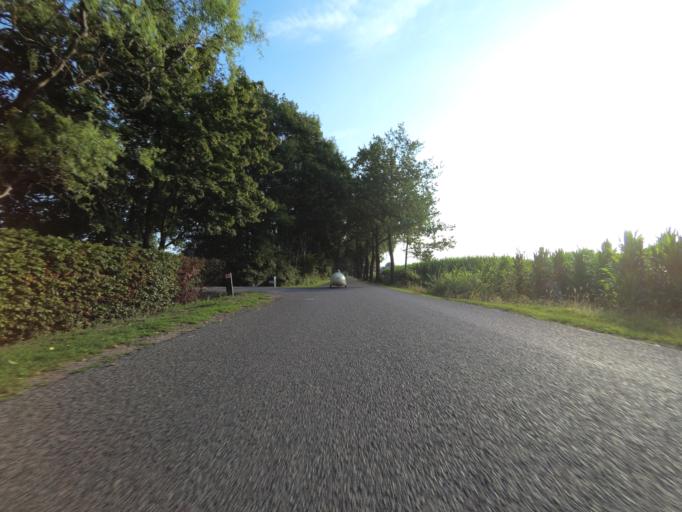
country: NL
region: Gelderland
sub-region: Gemeente Lochem
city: Harfsen
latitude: 52.2731
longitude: 6.3312
